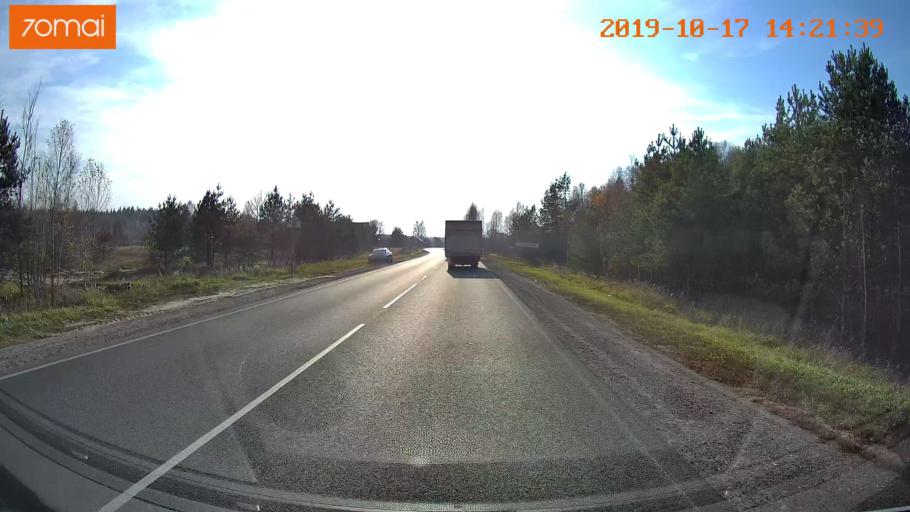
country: RU
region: Moskovskaya
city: Radovitskiy
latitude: 55.0363
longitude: 39.9762
